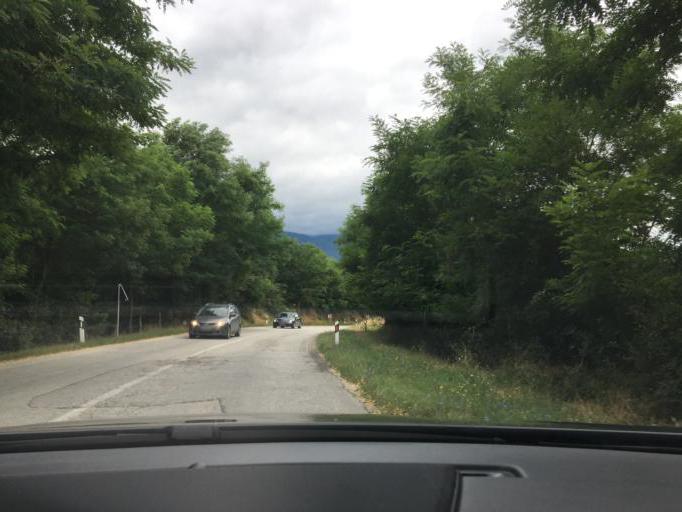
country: MK
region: Kriva Palanka
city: Kriva Palanka
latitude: 42.1813
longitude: 22.2762
